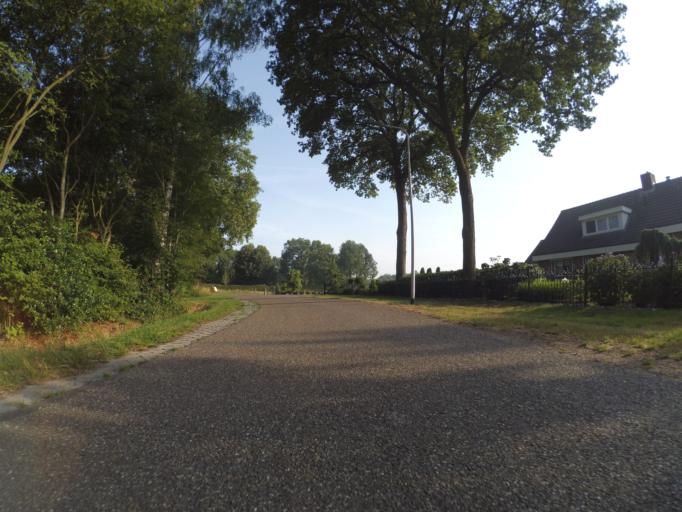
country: NL
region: Overijssel
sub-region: Gemeente Twenterand
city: Den Ham
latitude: 52.3736
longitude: 6.4925
